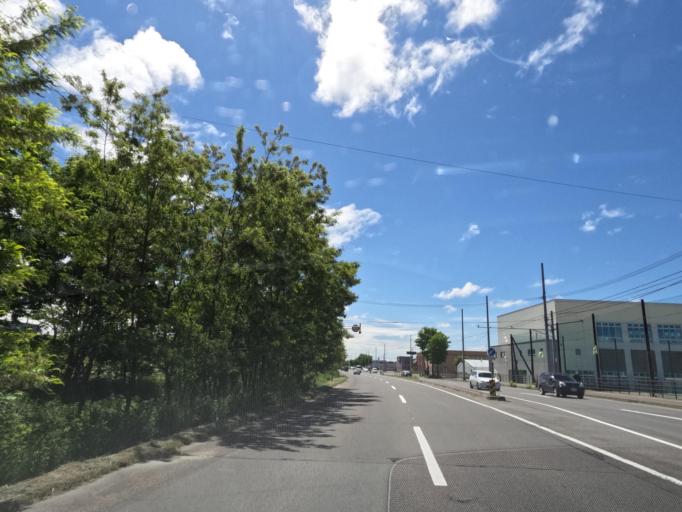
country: JP
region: Hokkaido
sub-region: Asahikawa-shi
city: Asahikawa
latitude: 43.7440
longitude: 142.3581
